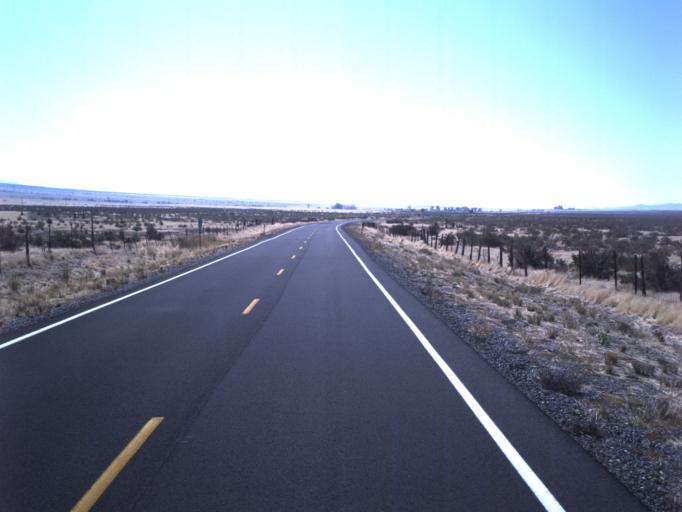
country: US
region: Utah
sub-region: Tooele County
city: Grantsville
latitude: 40.4864
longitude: -112.7462
